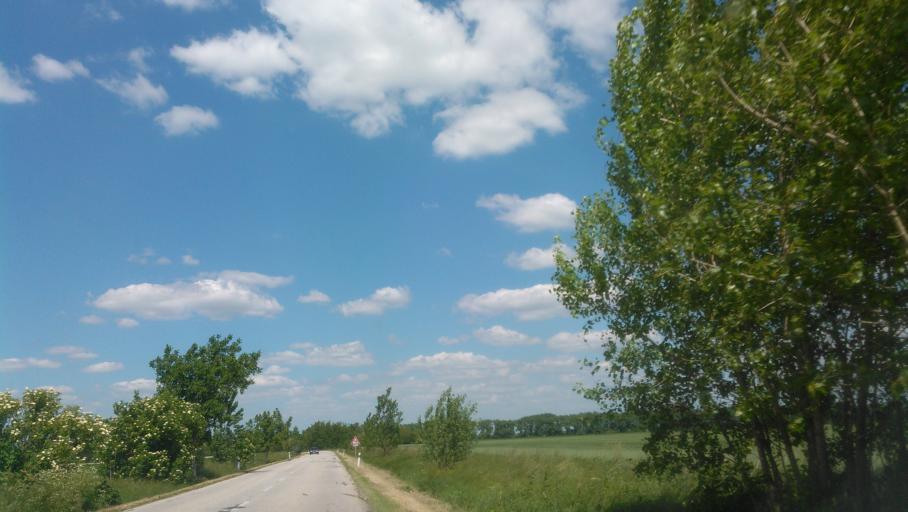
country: SK
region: Nitriansky
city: Kolarovo
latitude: 47.8825
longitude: 17.9218
